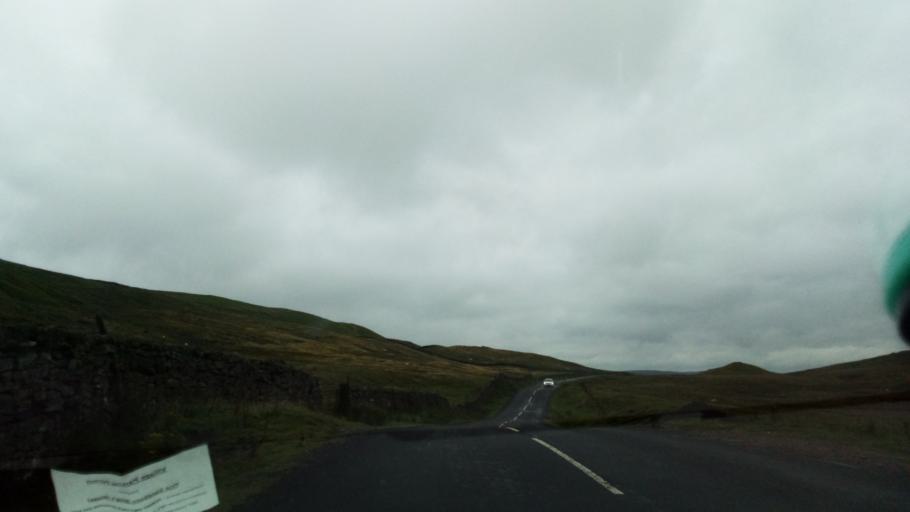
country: GB
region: England
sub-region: Cumbria
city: Kirkby Stephen
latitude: 54.5715
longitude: -2.2719
